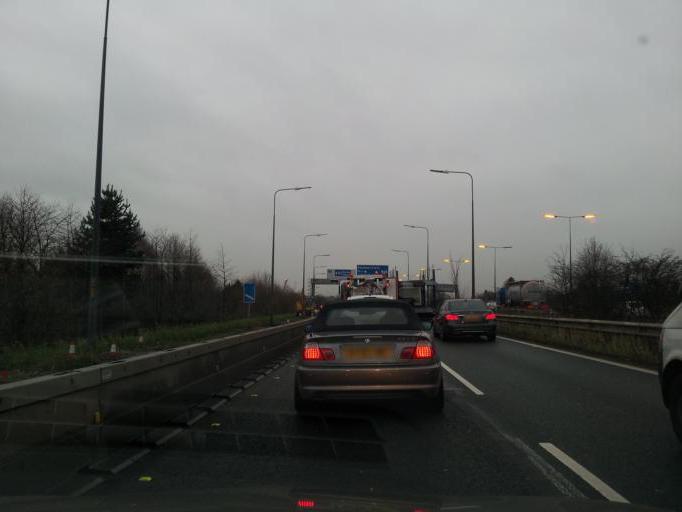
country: GB
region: England
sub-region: Manchester
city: Swinton
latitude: 53.4798
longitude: -2.3750
